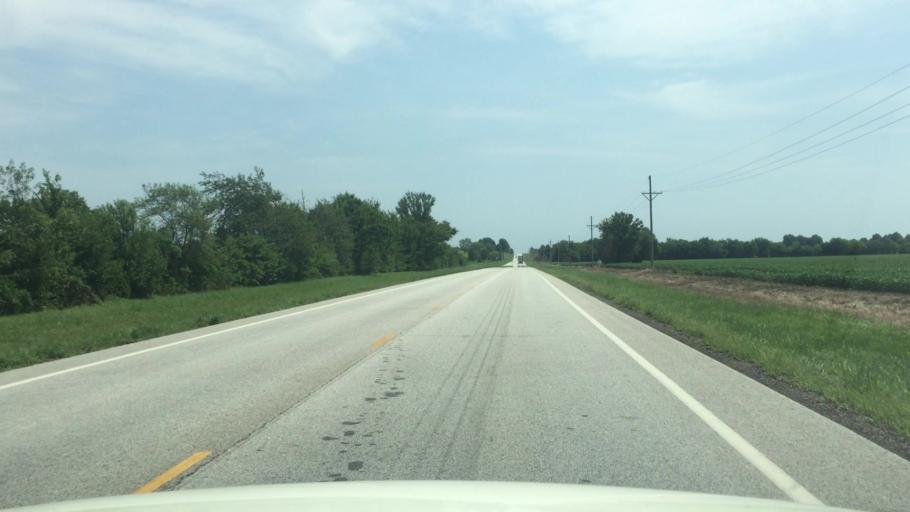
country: US
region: Kansas
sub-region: Cherokee County
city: Columbus
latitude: 37.1781
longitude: -94.8021
